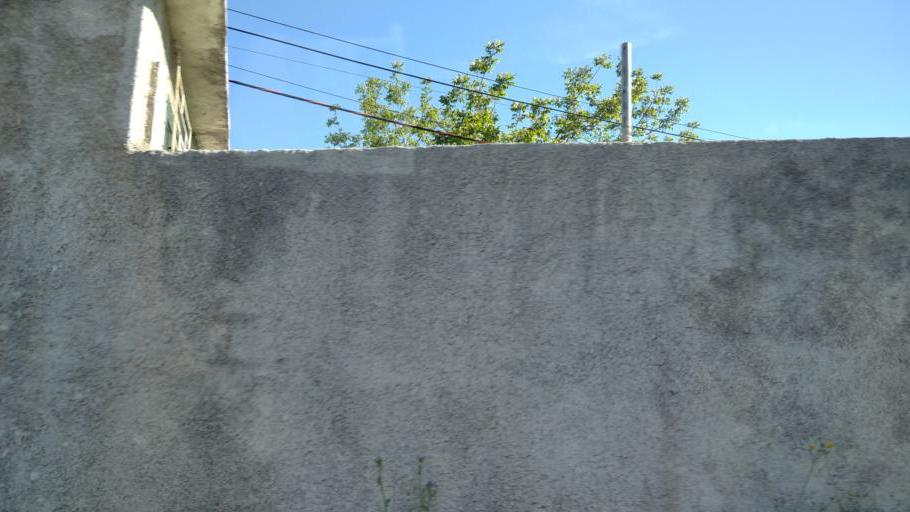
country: AL
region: Shkoder
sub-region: Rrethi i Shkodres
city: Shkoder
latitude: 42.0793
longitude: 19.5026
